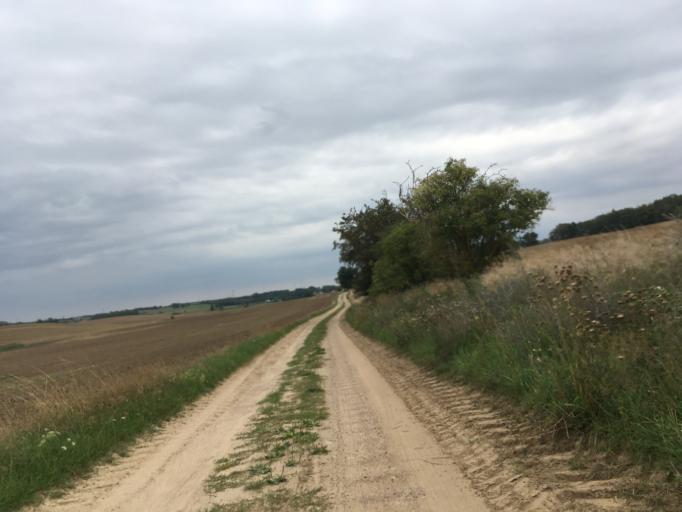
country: DE
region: Brandenburg
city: Angermunde
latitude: 53.0667
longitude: 14.0168
